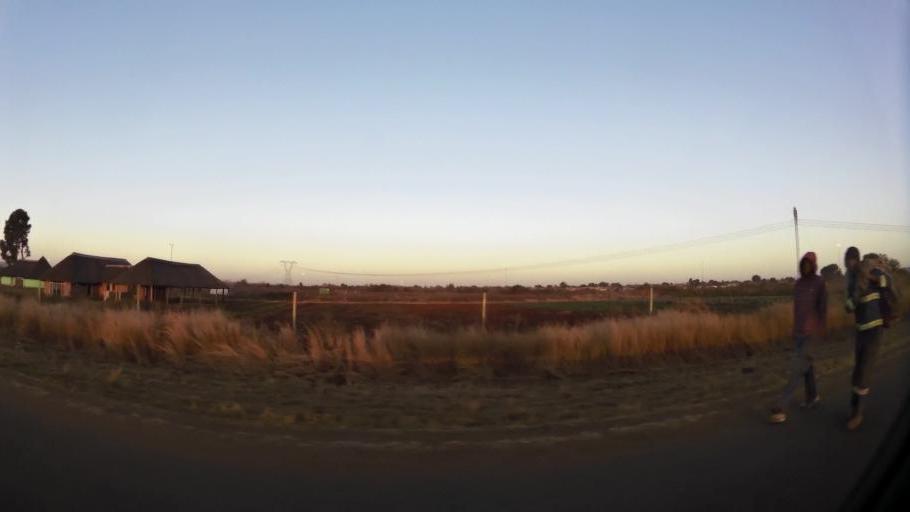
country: ZA
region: North-West
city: Ga-Rankuwa
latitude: -25.5802
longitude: 28.0482
